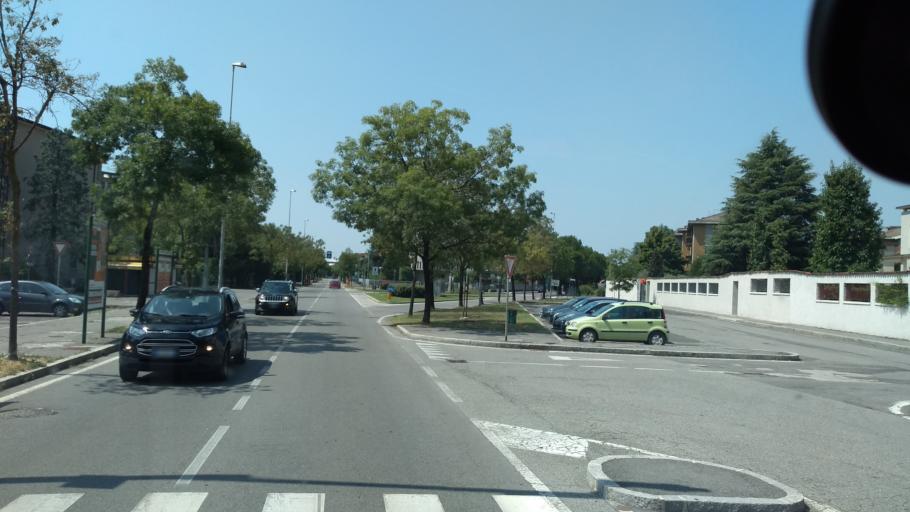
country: IT
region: Lombardy
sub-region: Provincia di Bergamo
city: Treviglio
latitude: 45.5193
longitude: 9.6056
